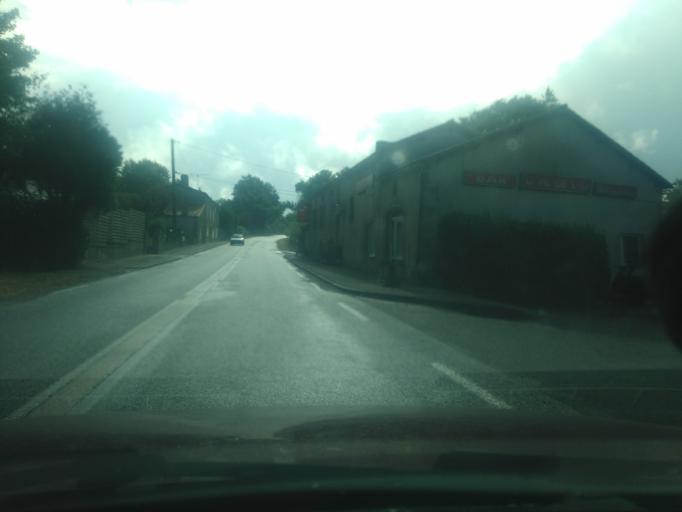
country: FR
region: Poitou-Charentes
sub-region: Departement des Deux-Sevres
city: Le Tallud
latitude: 46.6255
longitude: -0.3227
